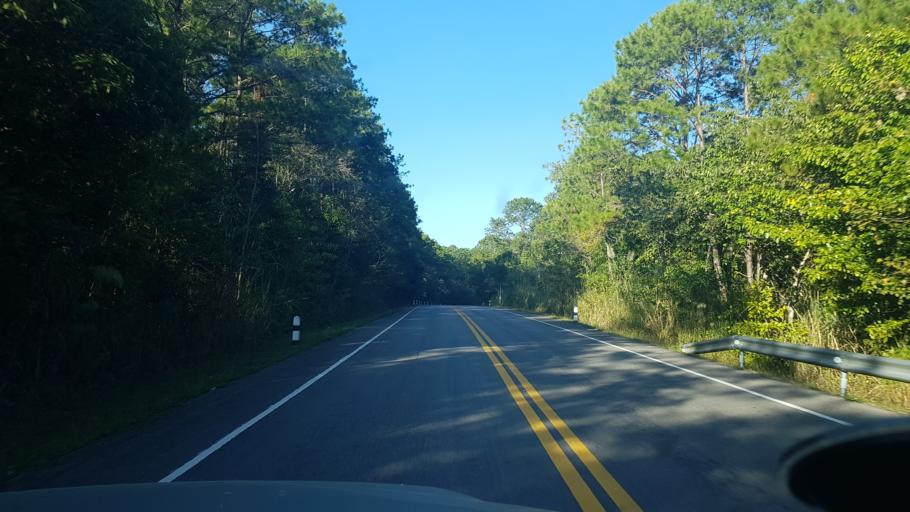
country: TH
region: Phetchabun
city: Nam Nao
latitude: 16.7286
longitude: 101.5665
